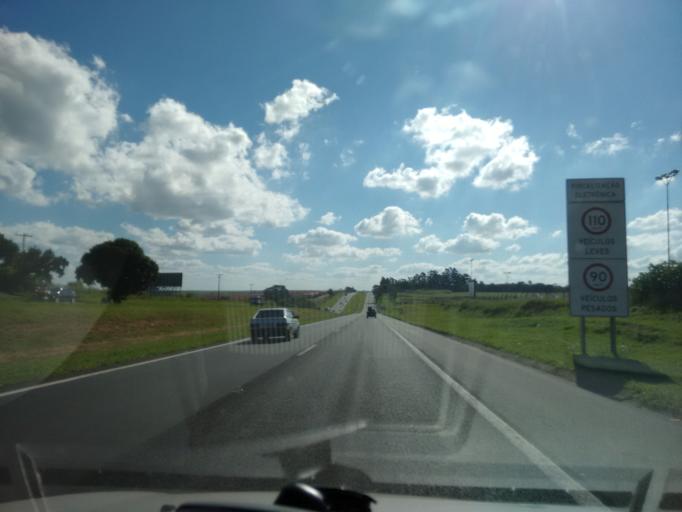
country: BR
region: Sao Paulo
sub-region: Ibate
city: Ibate
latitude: -21.9733
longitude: -47.9420
